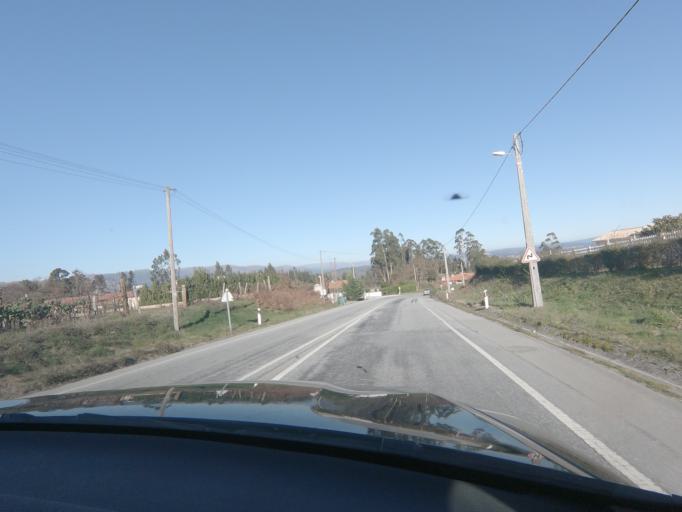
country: PT
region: Viseu
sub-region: Vouzela
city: Vouzela
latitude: 40.7179
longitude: -8.1335
